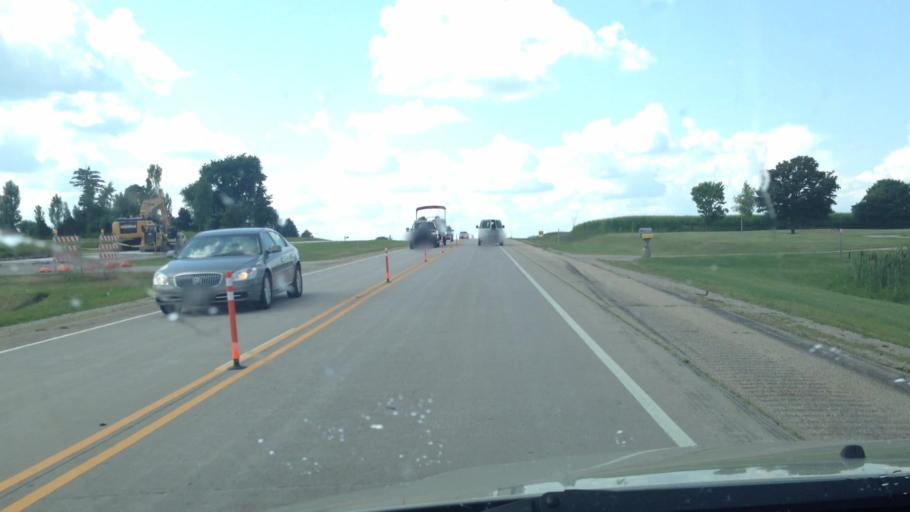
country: US
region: Wisconsin
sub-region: Shawano County
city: Bonduel
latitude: 44.6976
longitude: -88.3526
